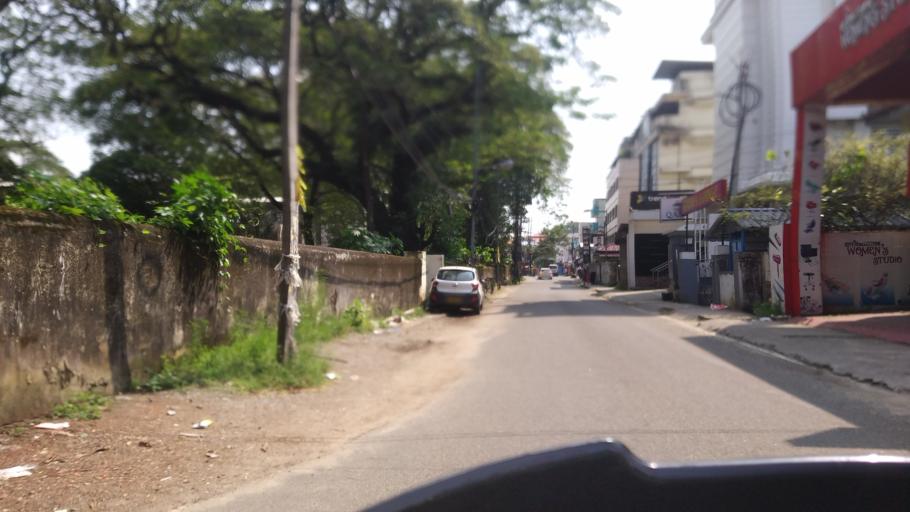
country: IN
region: Kerala
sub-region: Ernakulam
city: Cochin
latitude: 9.9747
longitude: 76.2808
